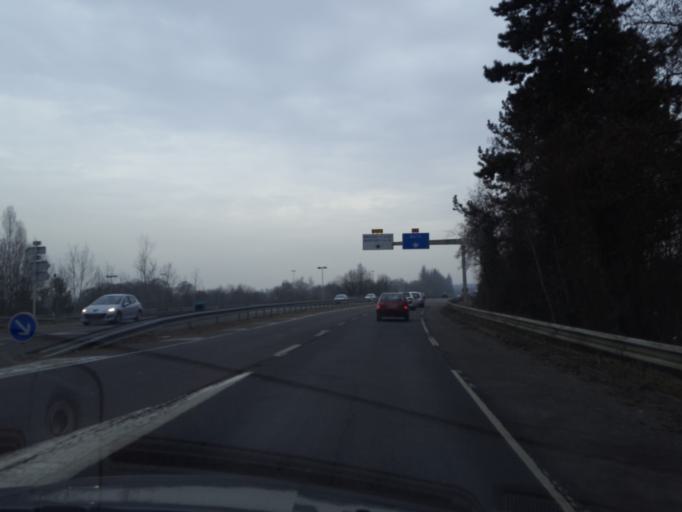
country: FR
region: Lorraine
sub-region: Departement de la Moselle
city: Moulins-les-Metz
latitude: 49.0982
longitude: 6.1178
